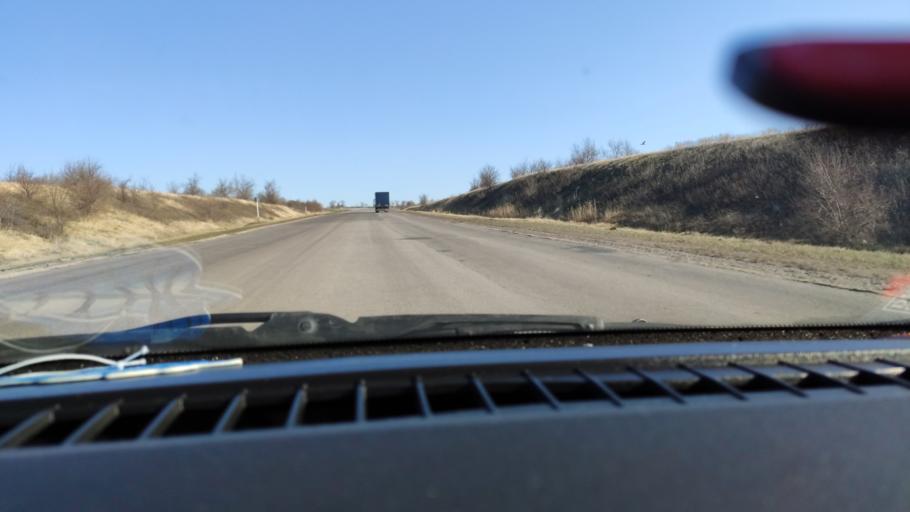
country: RU
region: Samara
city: Varlamovo
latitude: 53.0998
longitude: 48.3566
